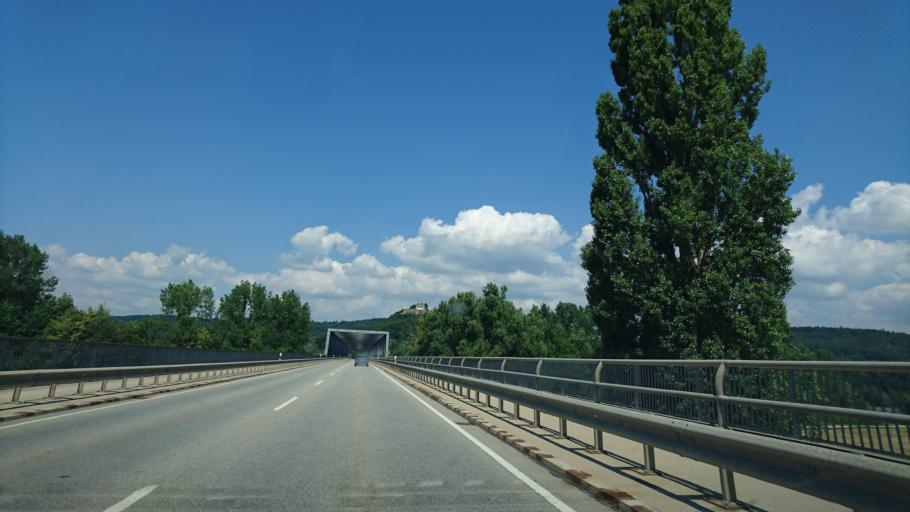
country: DE
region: Bavaria
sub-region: Upper Palatinate
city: Donaustauf
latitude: 49.0233
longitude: 12.2135
